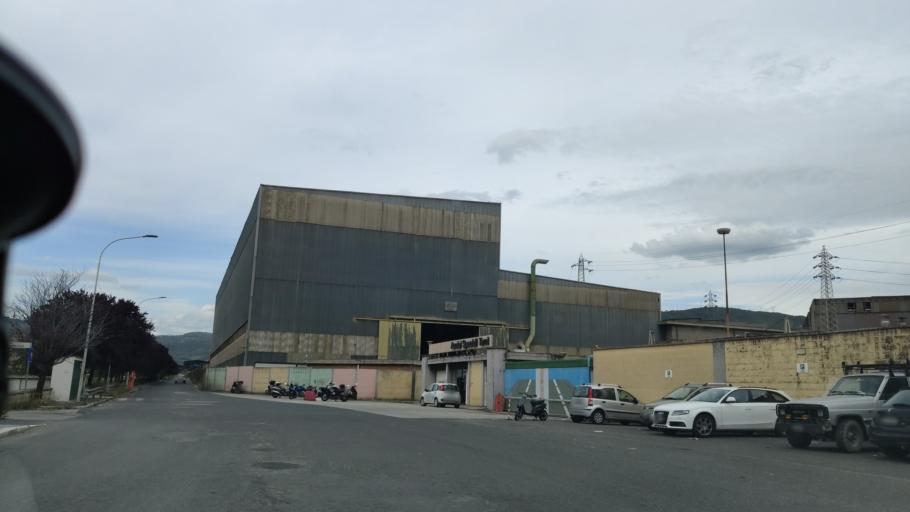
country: IT
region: Umbria
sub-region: Provincia di Terni
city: Terni
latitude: 42.5669
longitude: 12.6621
